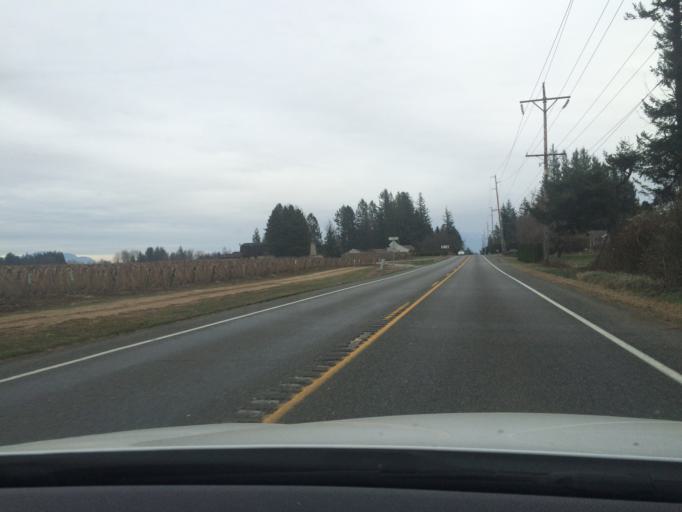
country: US
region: Washington
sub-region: Whatcom County
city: Lynden
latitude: 48.9641
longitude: -122.4171
